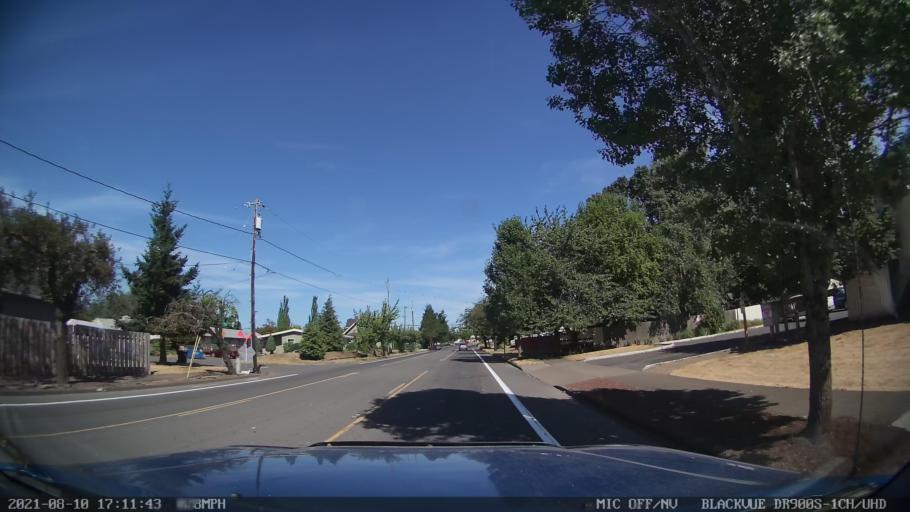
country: US
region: Oregon
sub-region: Marion County
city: Salem
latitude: 44.9619
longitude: -123.0181
